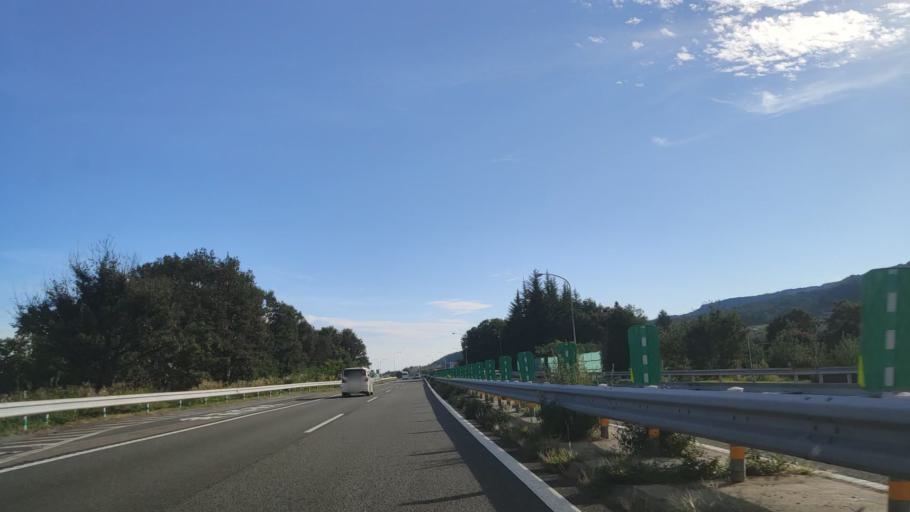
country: JP
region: Nagano
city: Iida
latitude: 35.6095
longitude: 137.8854
